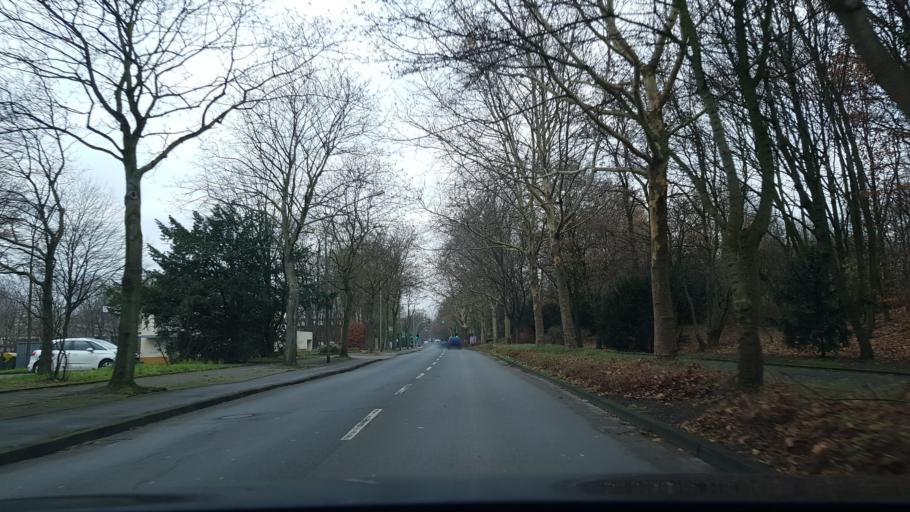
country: DE
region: North Rhine-Westphalia
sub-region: Regierungsbezirk Dusseldorf
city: Dinslaken
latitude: 51.5201
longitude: 6.7756
